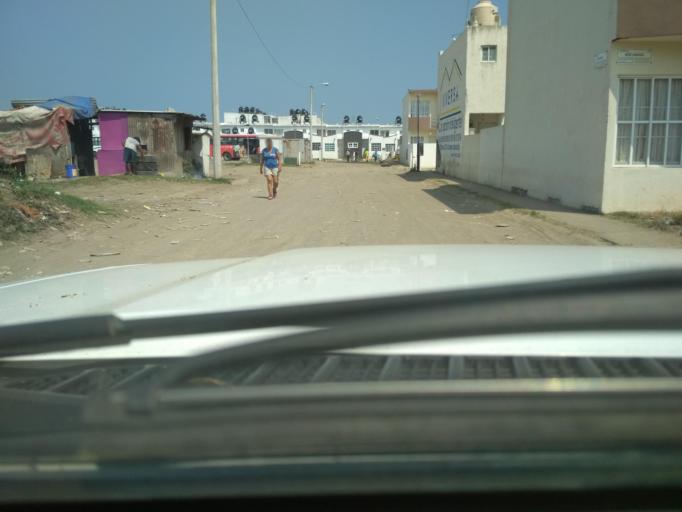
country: MX
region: Veracruz
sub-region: Veracruz
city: Lomas de Rio Medio Cuatro
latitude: 19.1854
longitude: -96.2086
